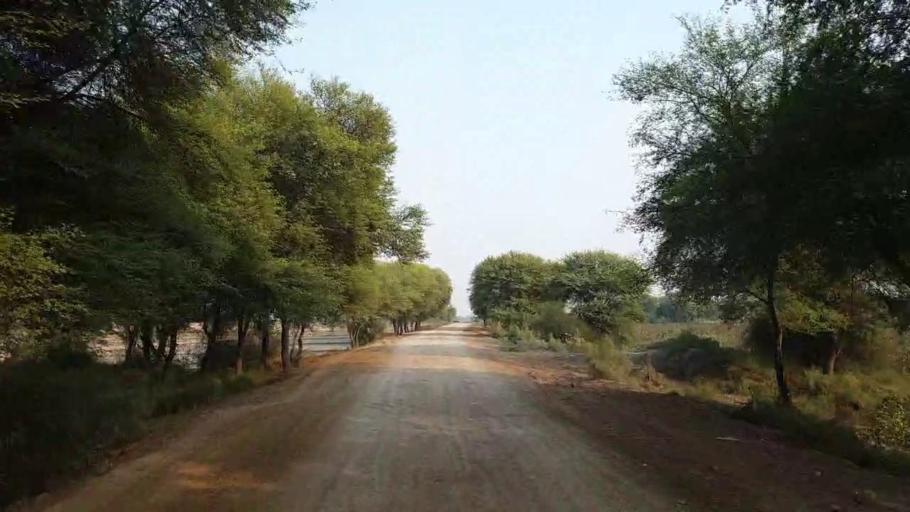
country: PK
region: Sindh
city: Bhan
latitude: 26.5015
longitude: 67.7612
